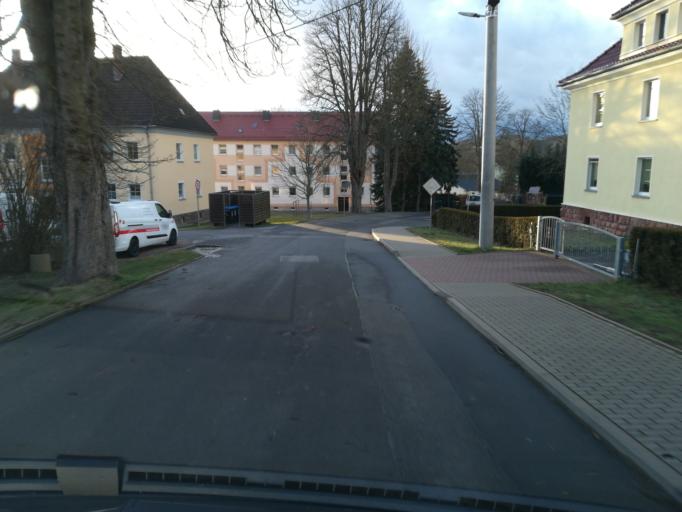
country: DE
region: Saxony
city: Wechselburg
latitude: 51.0014
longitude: 12.7772
